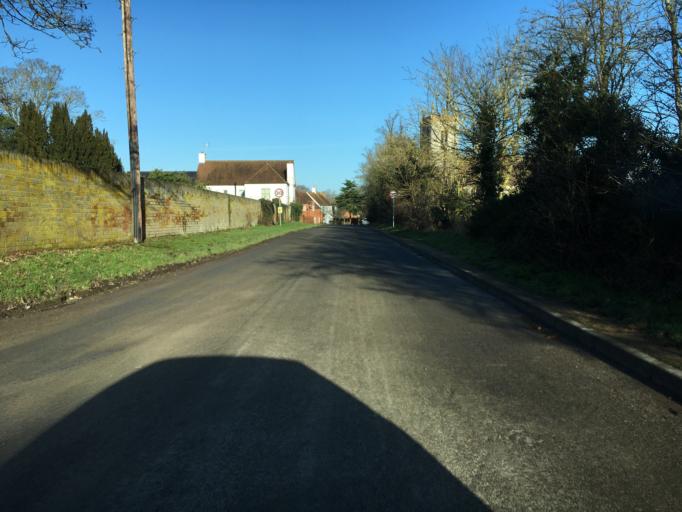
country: GB
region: England
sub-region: Warwickshire
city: Stratford-upon-Avon
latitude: 52.2037
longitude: -1.6626
